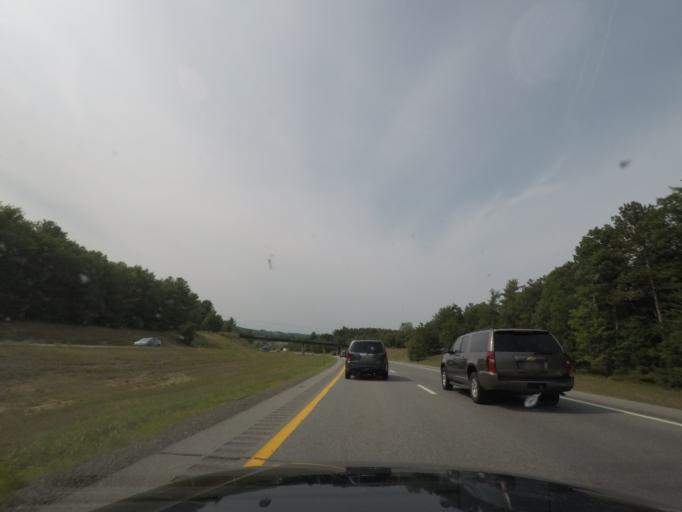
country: US
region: New York
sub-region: Essex County
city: Keeseville
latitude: 44.4869
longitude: -73.4898
